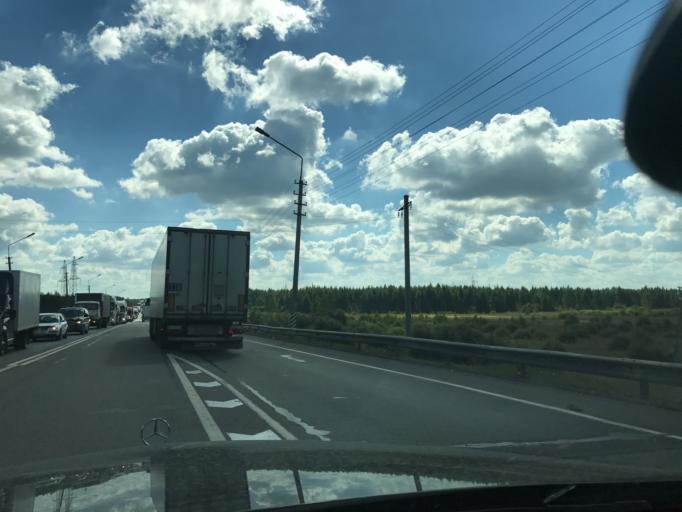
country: RU
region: Vladimir
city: Vorsha
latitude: 56.0795
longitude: 40.2019
